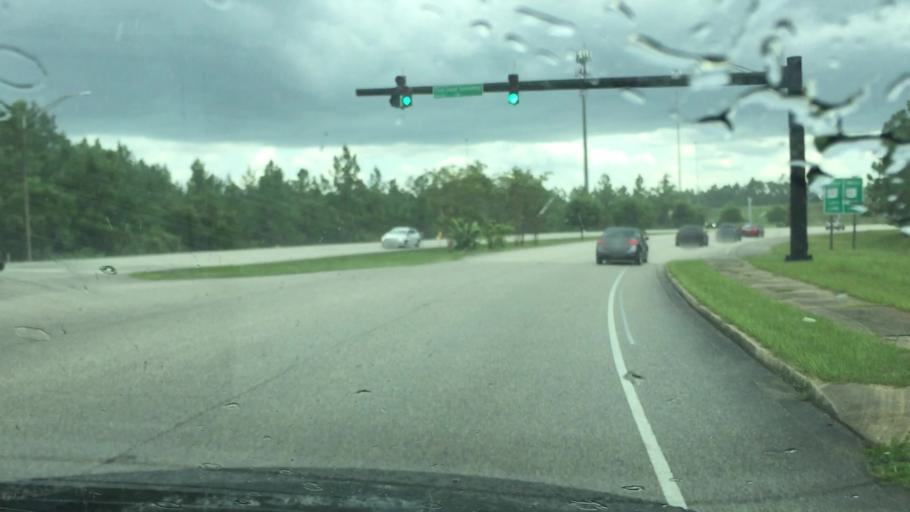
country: US
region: Florida
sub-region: Duval County
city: Jacksonville Beach
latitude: 30.2552
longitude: -81.4979
